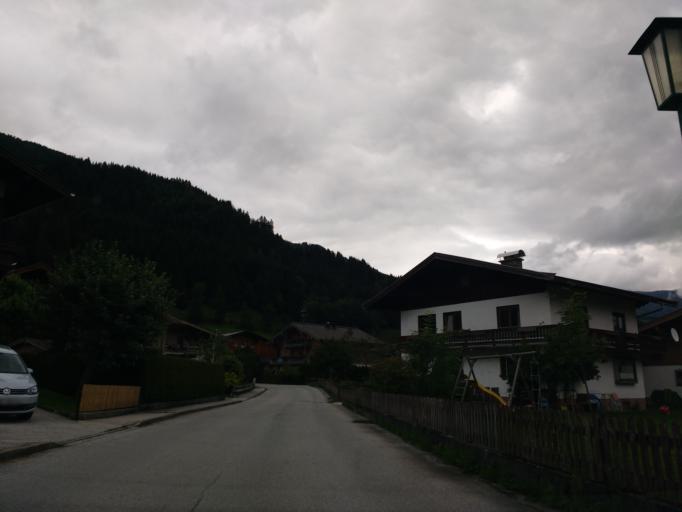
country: AT
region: Salzburg
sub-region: Politischer Bezirk Zell am See
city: Hollersbach im Pinzgau
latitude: 47.2795
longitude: 12.3868
